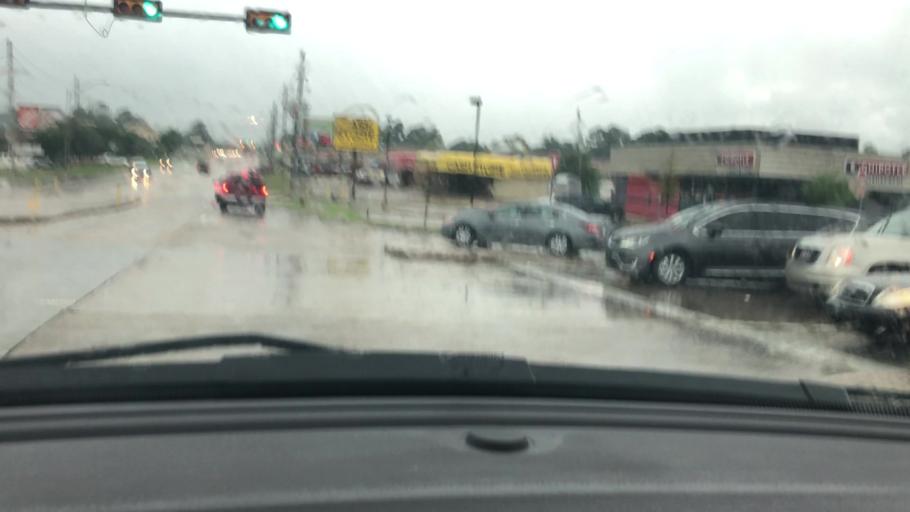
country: US
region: Texas
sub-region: Bowie County
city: Wake Village
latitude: 33.4574
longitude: -94.0877
